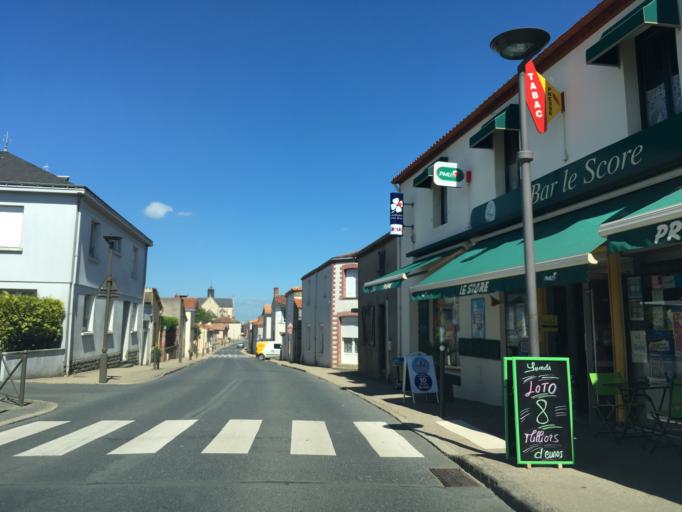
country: FR
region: Pays de la Loire
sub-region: Departement de la Vendee
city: Saint-Georges-de-Montaigu
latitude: 46.9456
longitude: -1.2917
